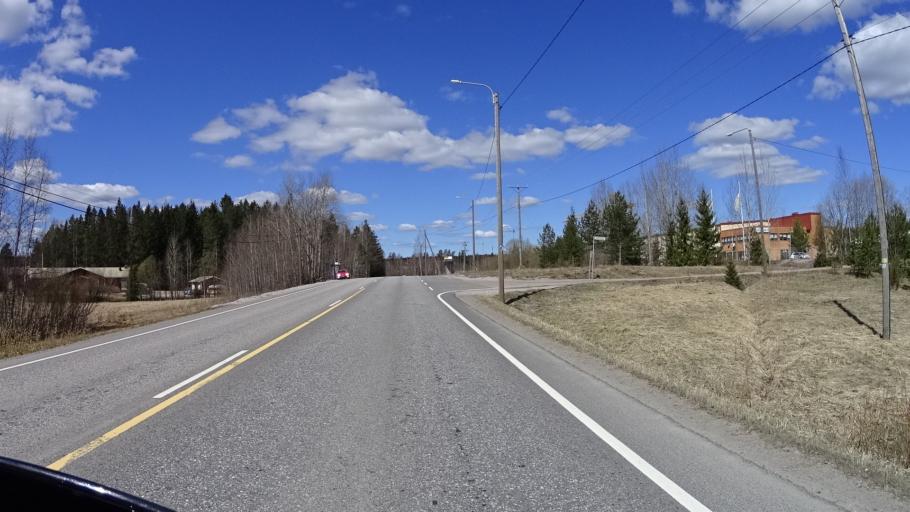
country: FI
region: Uusimaa
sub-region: Helsinki
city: Kirkkonummi
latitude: 60.2646
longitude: 24.4689
